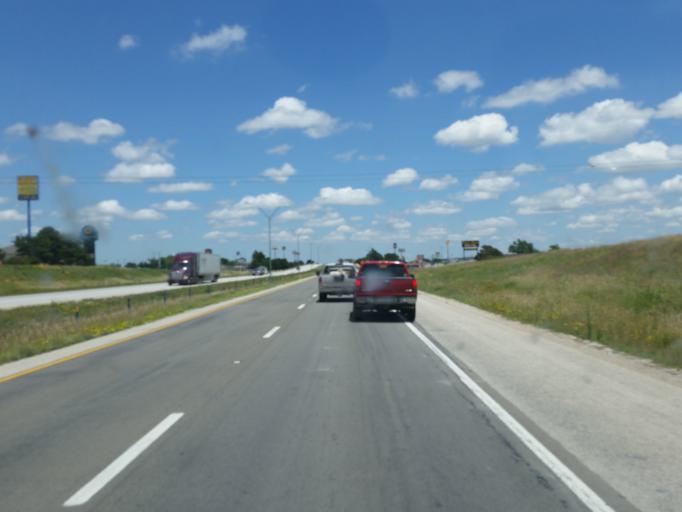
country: US
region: Texas
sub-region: Nolan County
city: Sweetwater
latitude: 32.4488
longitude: -100.4045
